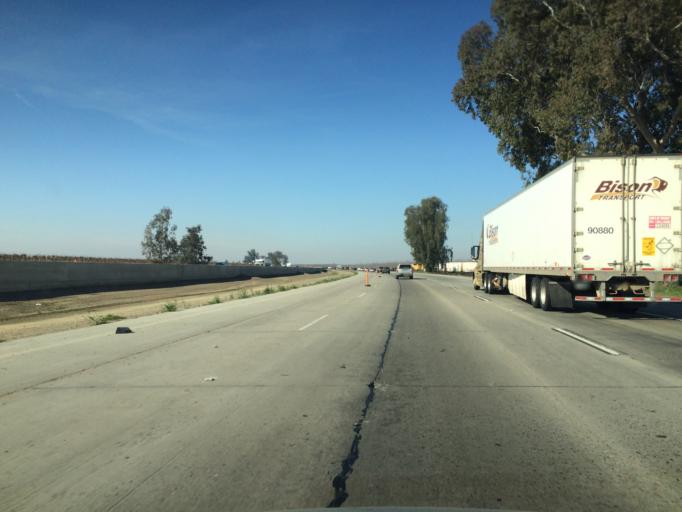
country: US
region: California
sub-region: Tulare County
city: Goshen
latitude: 36.3610
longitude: -119.4288
